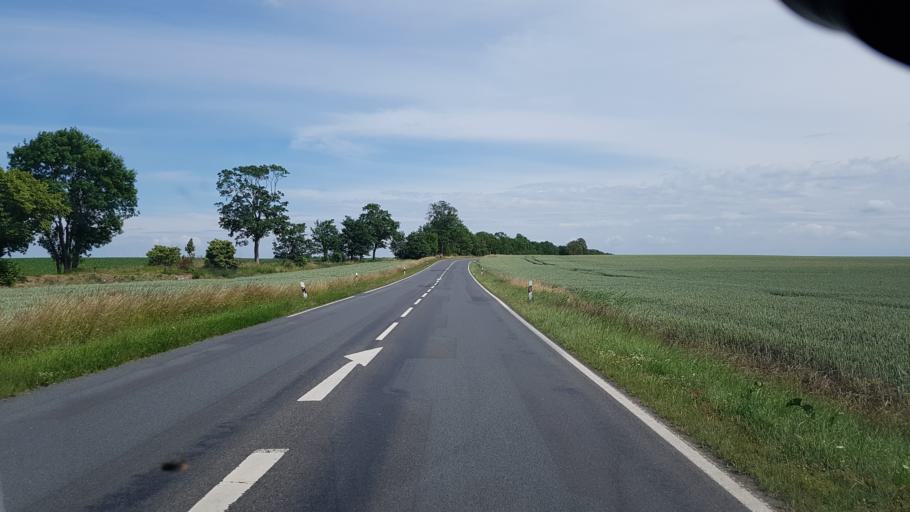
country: DE
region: Brandenburg
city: Prenzlau
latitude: 53.3216
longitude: 13.7906
